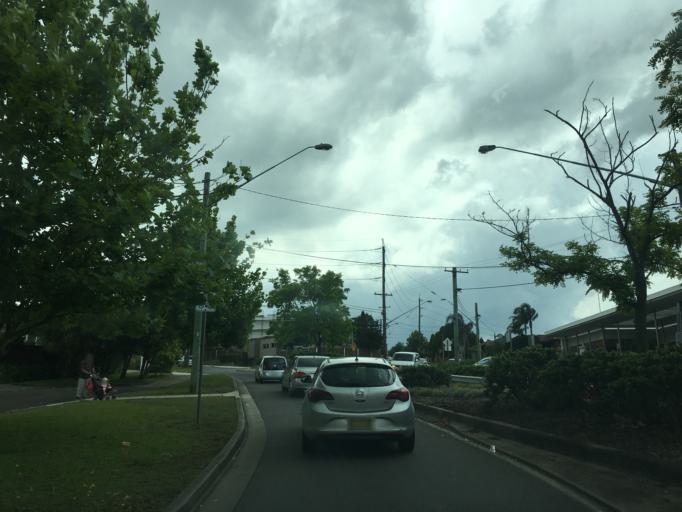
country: AU
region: New South Wales
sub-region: Ryde
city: Denistone
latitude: -33.7958
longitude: 151.1023
